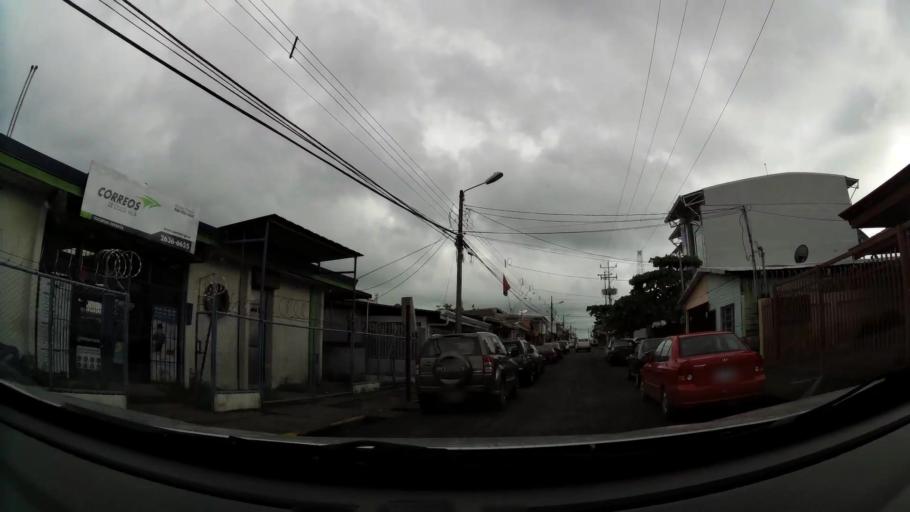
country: CR
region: Puntarenas
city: Esparza
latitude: 9.9920
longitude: -84.6682
